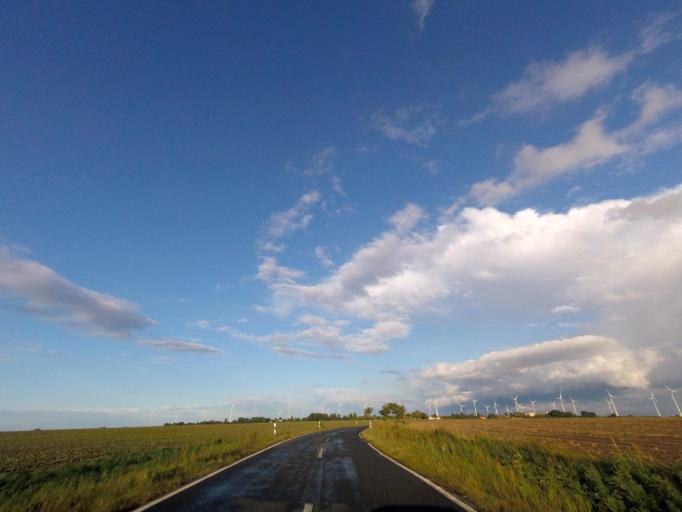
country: DE
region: Saxony-Anhalt
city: Kropstadt
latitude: 52.0088
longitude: 12.8049
